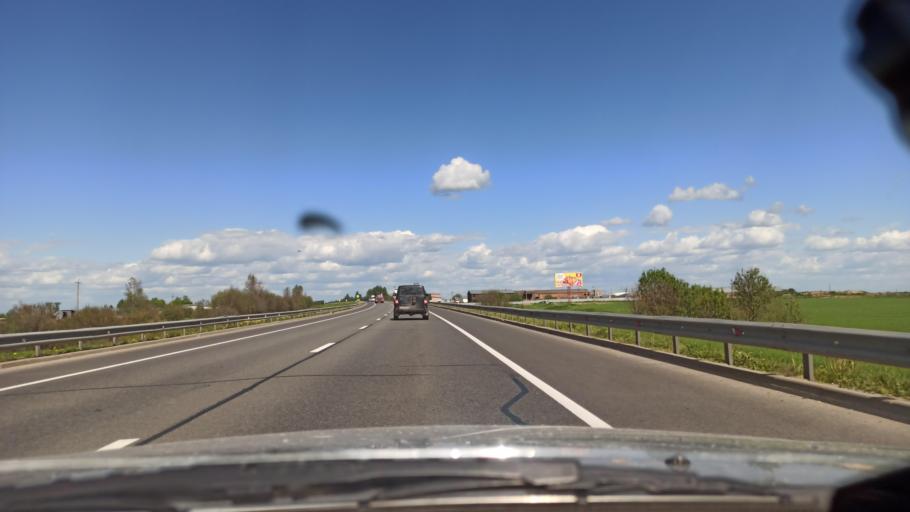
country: RU
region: Vologda
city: Vologda
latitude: 59.2788
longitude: 39.8302
